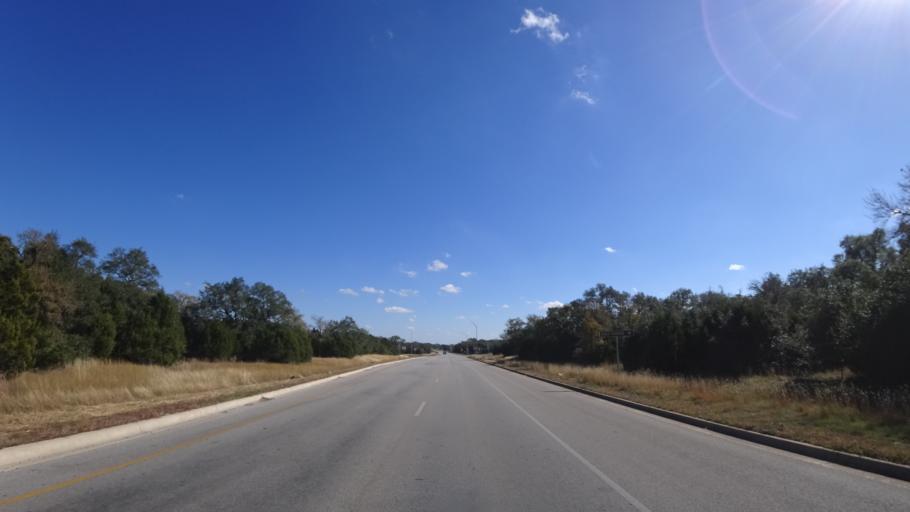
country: US
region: Texas
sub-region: Travis County
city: Shady Hollow
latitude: 30.1873
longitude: -97.9151
